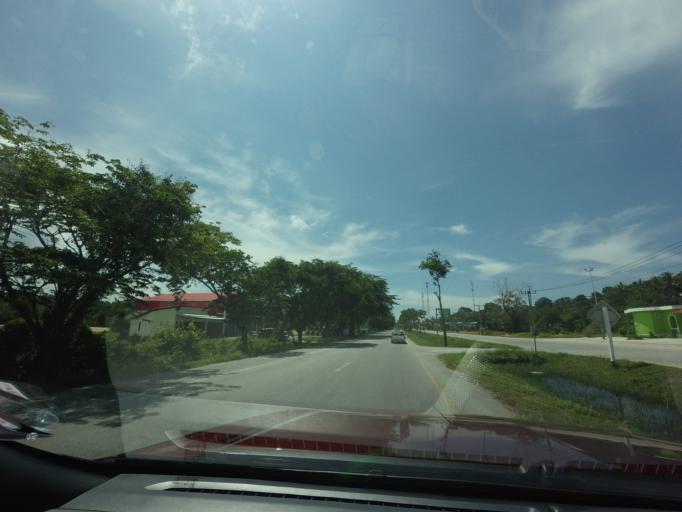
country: TH
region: Pattani
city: Mai Kaen
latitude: 6.6028
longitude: 101.6316
